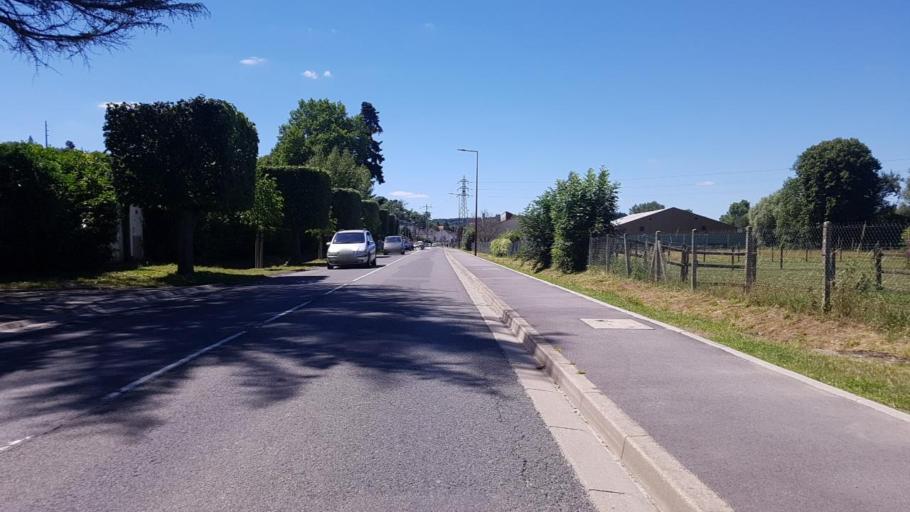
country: FR
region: Ile-de-France
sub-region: Departement de Seine-et-Marne
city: La Ferte-sous-Jouarre
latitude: 48.9544
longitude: 3.1399
